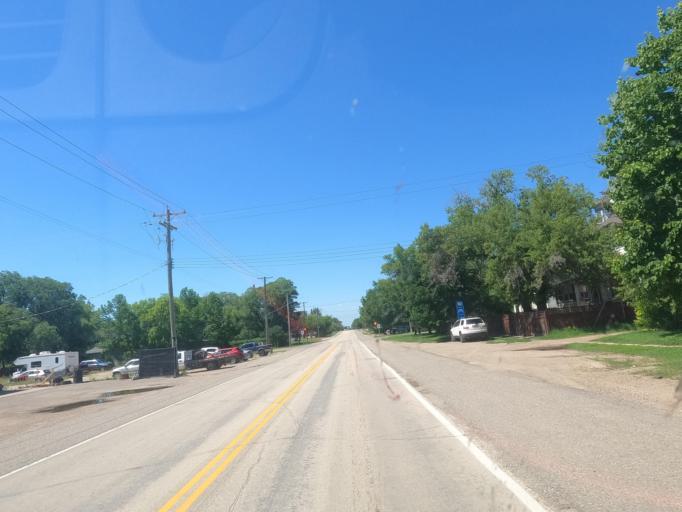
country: CA
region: Manitoba
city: Souris
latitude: 49.6211
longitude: -100.2614
